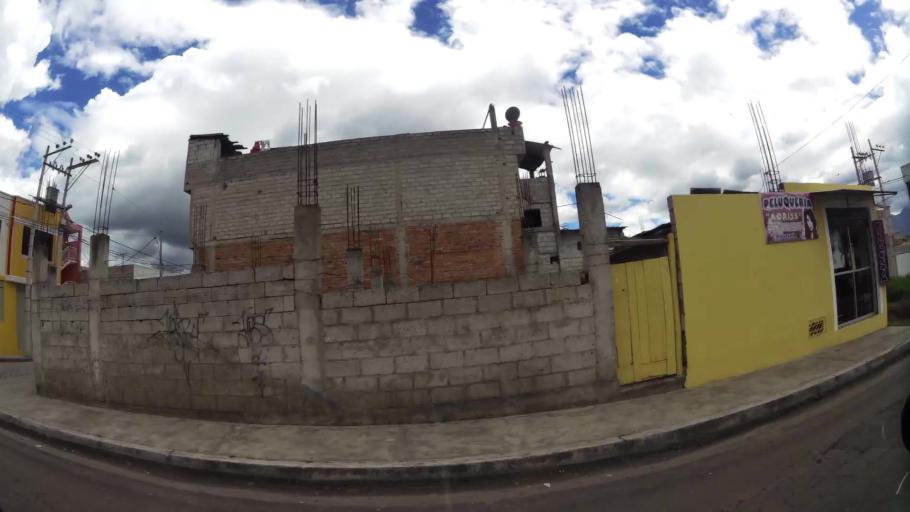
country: EC
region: Pichincha
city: Sangolqui
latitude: -0.3302
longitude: -78.5353
